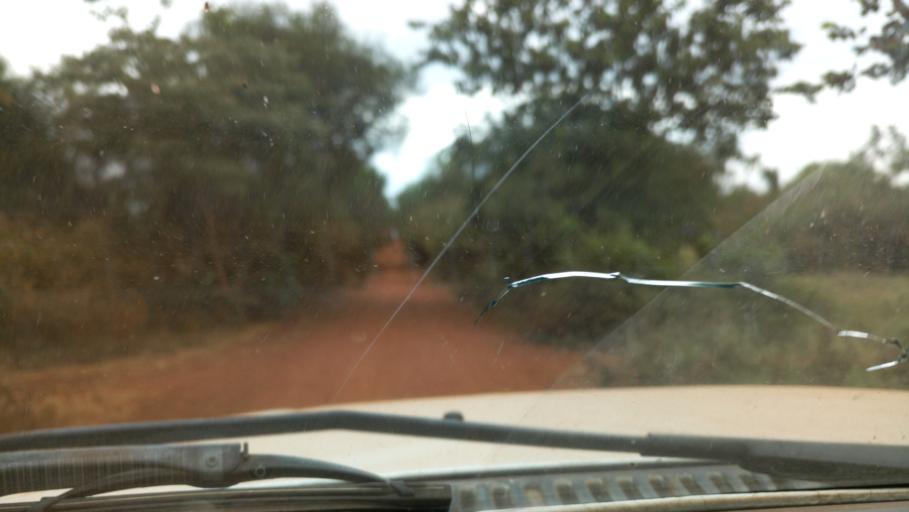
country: KE
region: Murang'a District
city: Karuri
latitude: -0.7665
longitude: 37.2339
